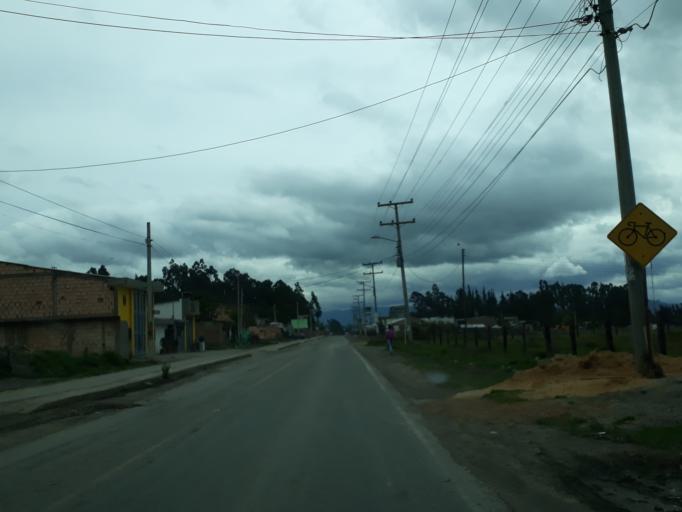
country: CO
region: Cundinamarca
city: Simijaca
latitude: 5.5094
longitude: -73.8460
